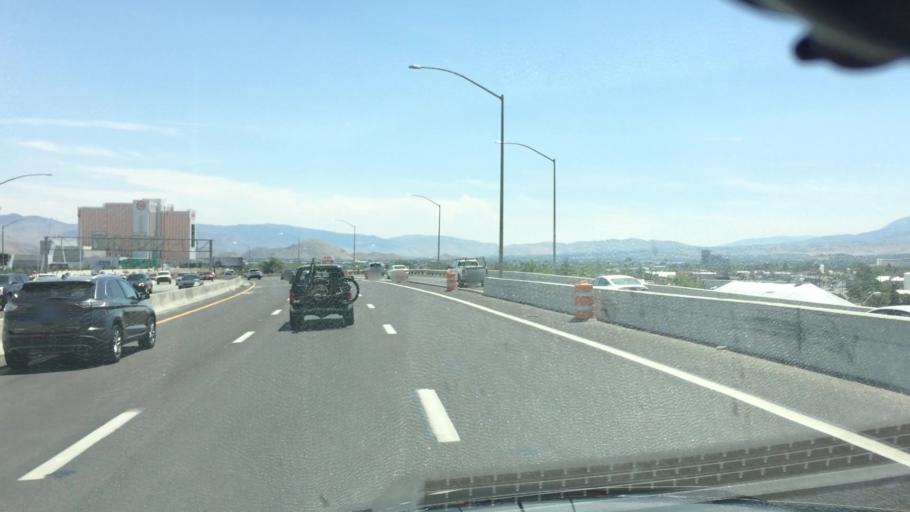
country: US
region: Nevada
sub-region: Washoe County
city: Reno
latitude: 39.5333
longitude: -119.7875
